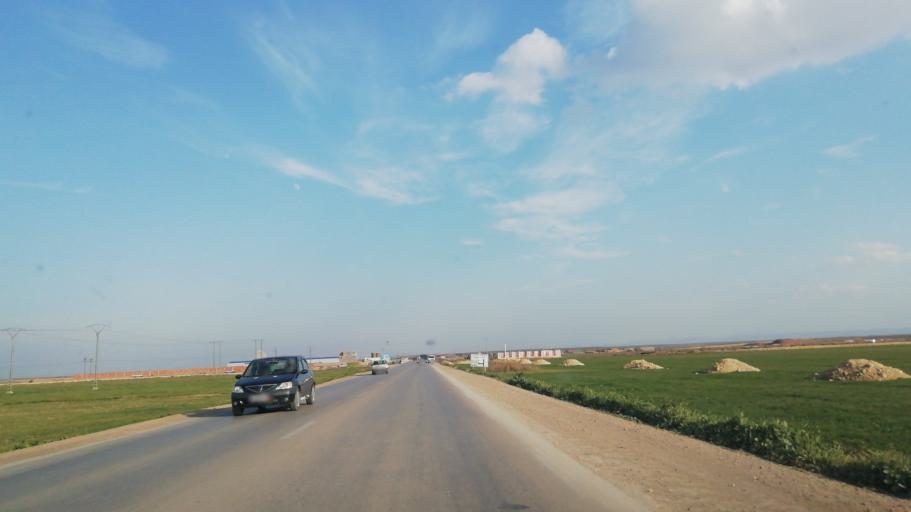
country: DZ
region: Relizane
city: Relizane
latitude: 35.8978
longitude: 0.5693
